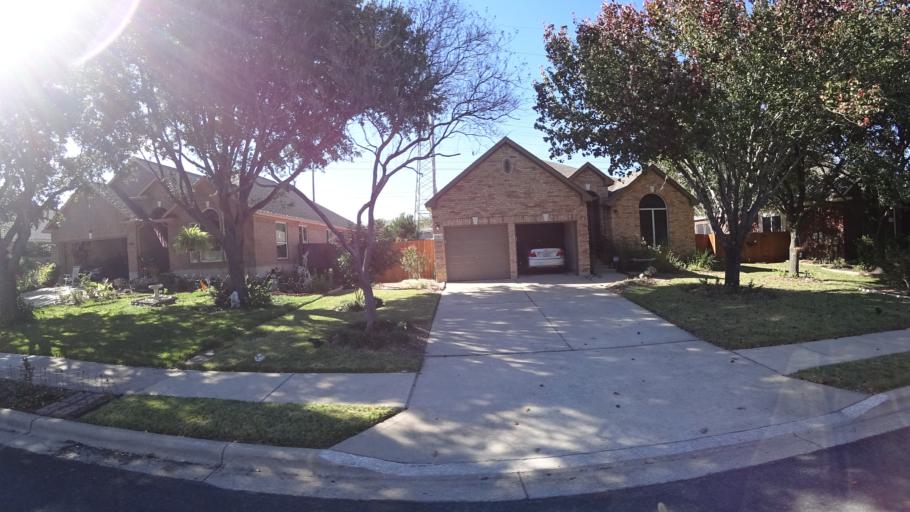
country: US
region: Texas
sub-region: Travis County
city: Wells Branch
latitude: 30.4266
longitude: -97.6878
